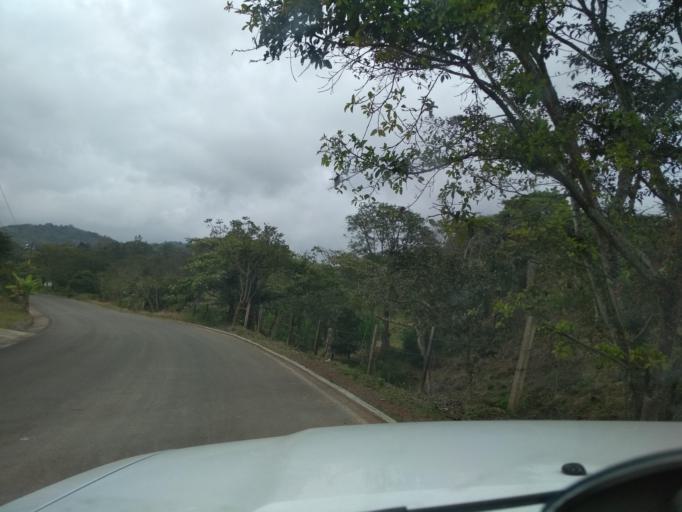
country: MX
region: Veracruz
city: El Castillo
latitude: 19.5480
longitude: -96.8468
